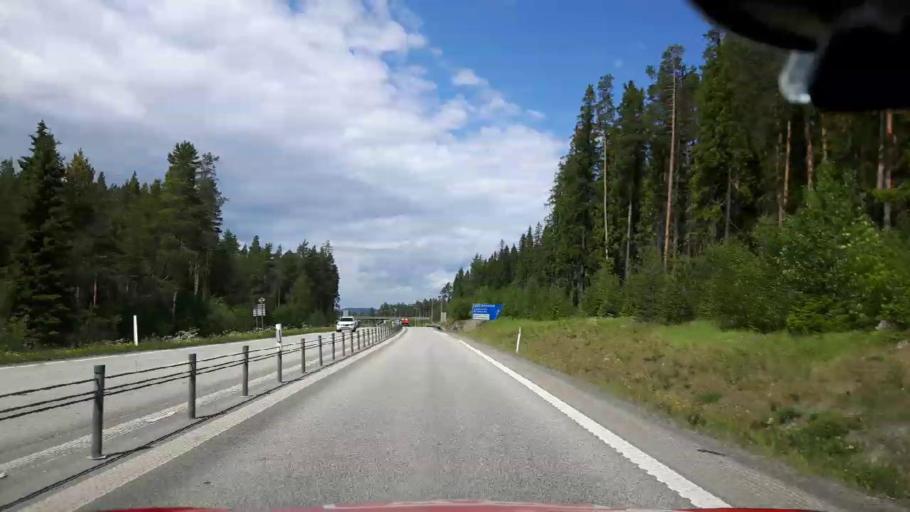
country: SE
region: Jaemtland
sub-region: OEstersunds Kommun
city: Ostersund
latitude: 63.1989
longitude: 14.6839
